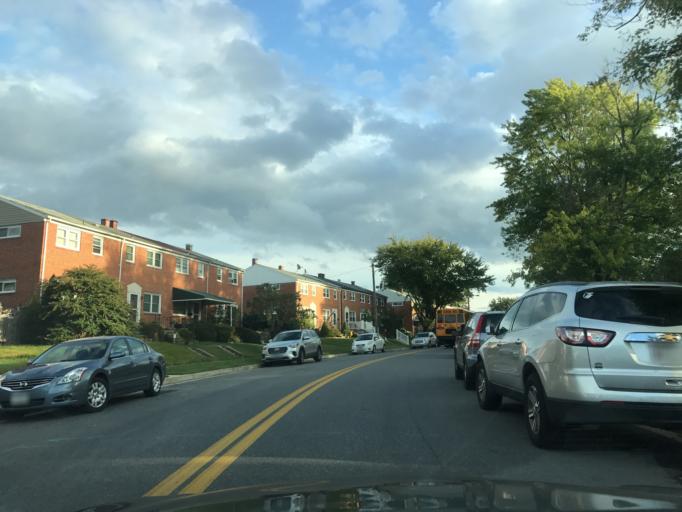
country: US
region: Maryland
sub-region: Baltimore County
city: Parkville
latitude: 39.3883
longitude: -76.5485
